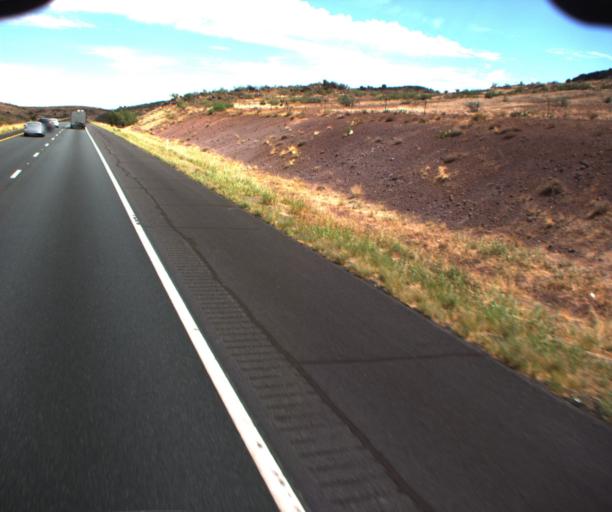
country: US
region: Arizona
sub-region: Yavapai County
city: Cordes Lakes
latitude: 34.4536
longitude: -112.0305
